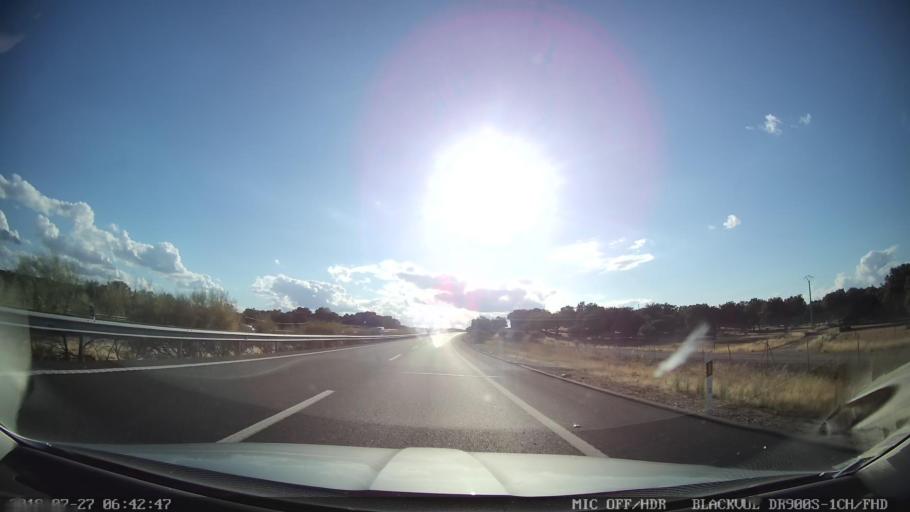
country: ES
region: Extremadura
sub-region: Provincia de Caceres
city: Peraleda de la Mata
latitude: 39.8894
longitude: -5.4911
